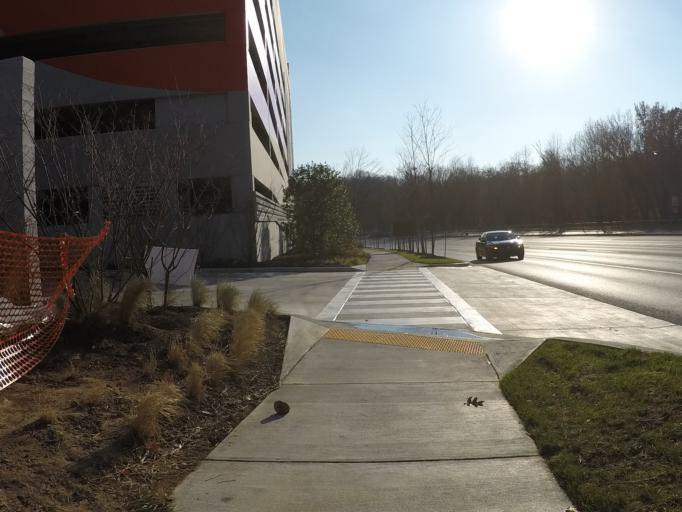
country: US
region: Maryland
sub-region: Howard County
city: Columbia
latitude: 39.2110
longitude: -76.8670
